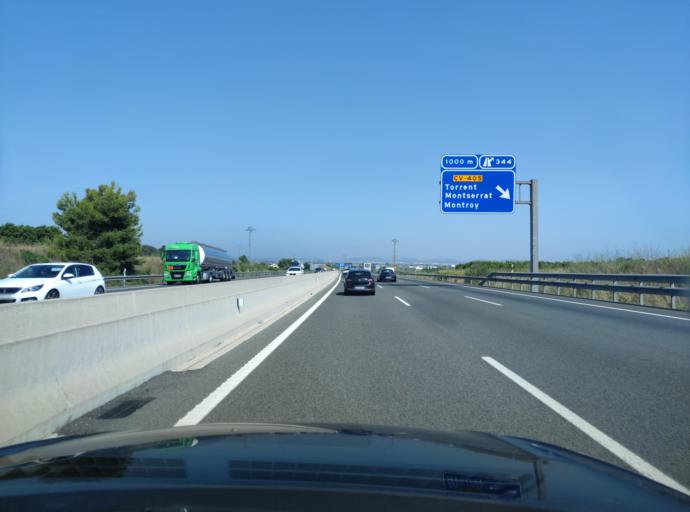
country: ES
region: Valencia
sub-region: Provincia de Valencia
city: Torrent
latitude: 39.4094
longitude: -0.4984
